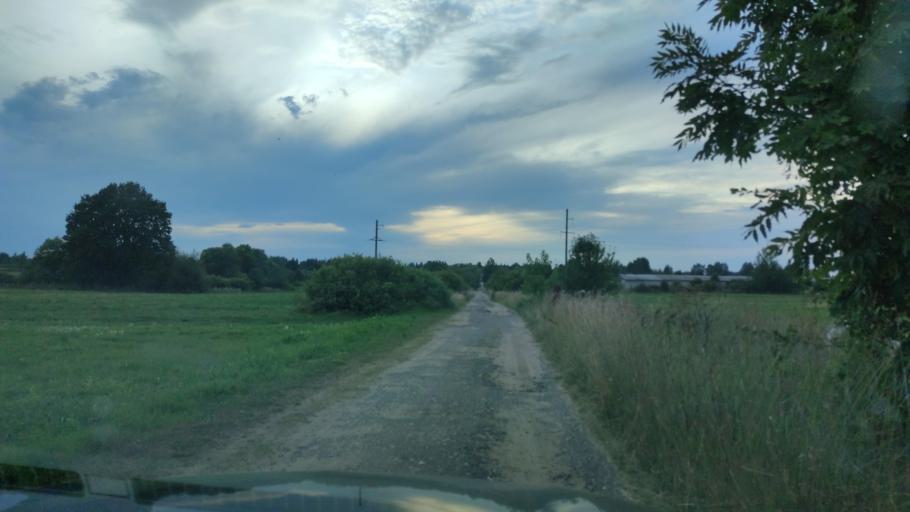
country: BY
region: Vitebsk
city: Mosar
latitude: 55.1261
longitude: 27.1674
